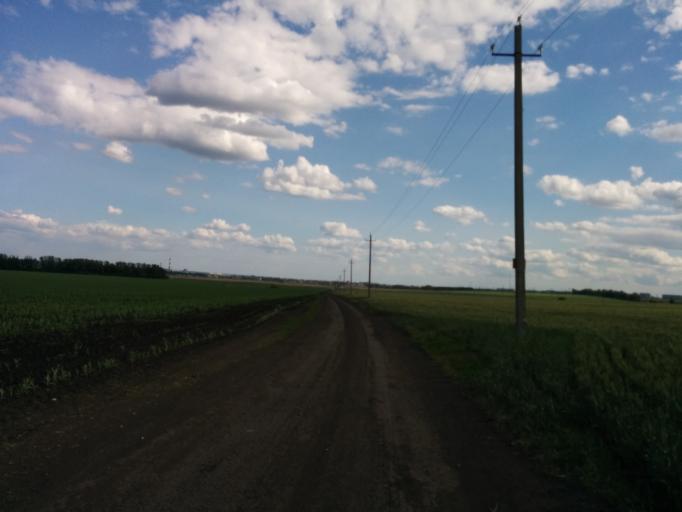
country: RU
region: Tambov
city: Donskoye
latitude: 52.7984
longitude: 41.4264
